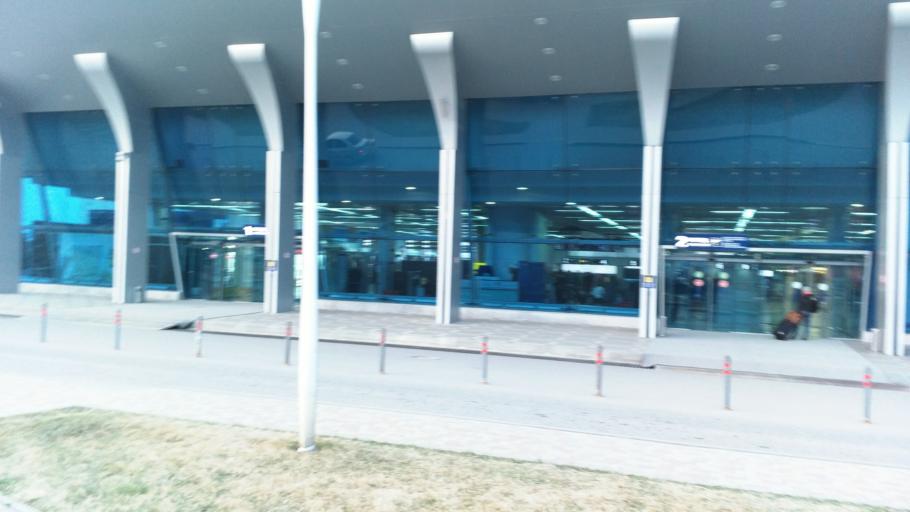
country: RU
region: Stavropol'skiy
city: Andzhiyevskiy
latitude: 44.2171
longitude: 43.0872
